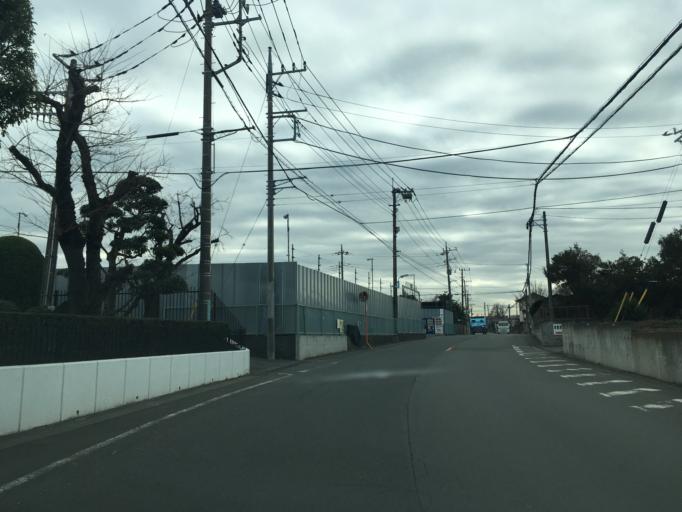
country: JP
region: Saitama
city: Sayama
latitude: 35.8011
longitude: 139.3962
